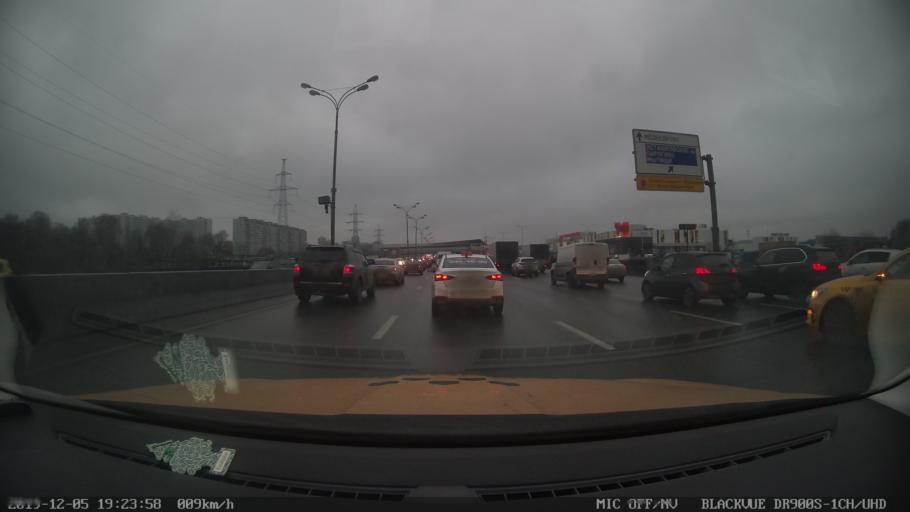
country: RU
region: Moscow
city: Vatutino
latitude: 55.8944
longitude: 37.6876
